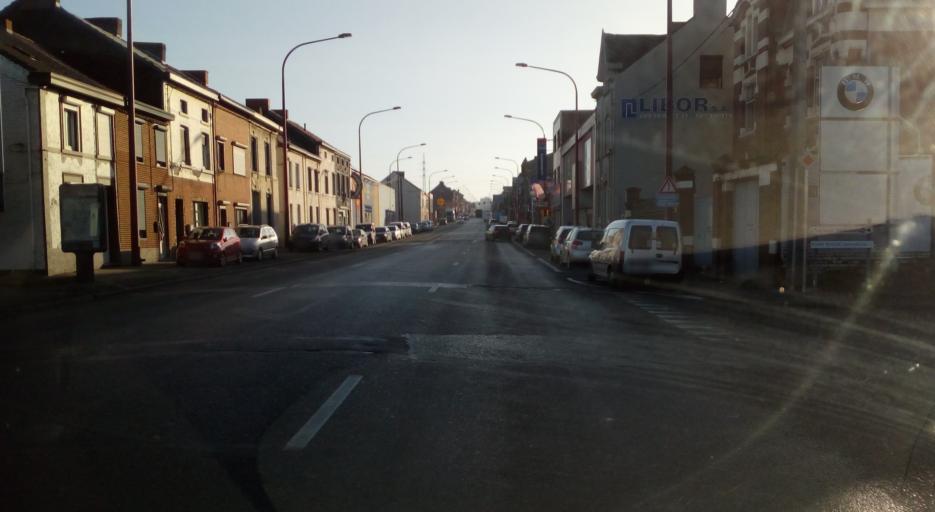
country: BE
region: Wallonia
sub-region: Province du Hainaut
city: Charleroi
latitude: 50.3950
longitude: 4.4563
